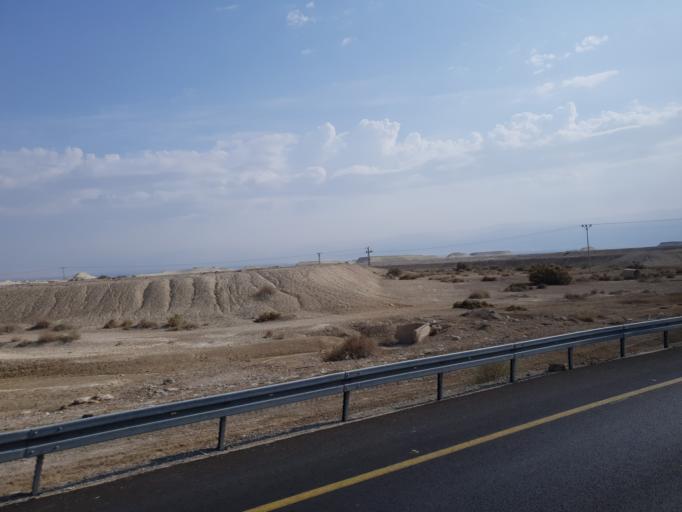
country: PS
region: West Bank
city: Jericho
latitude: 31.7959
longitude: 35.4958
